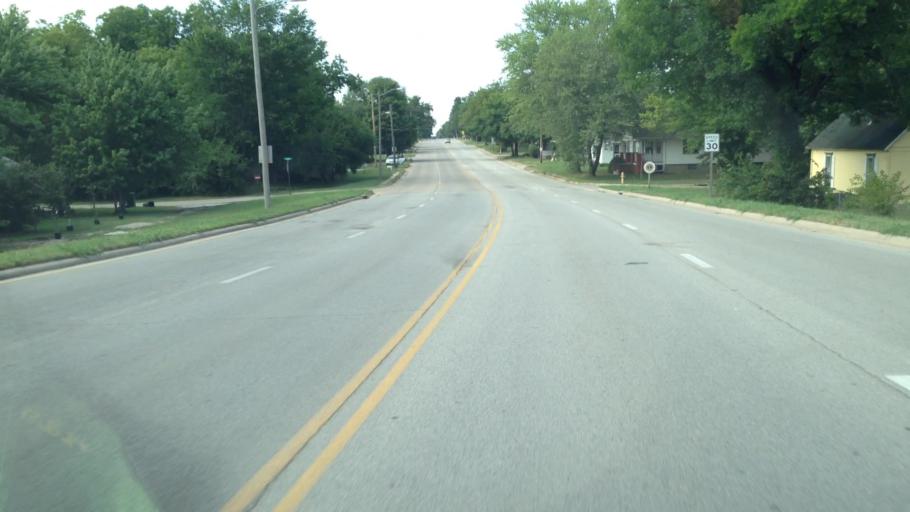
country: US
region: Kansas
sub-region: Labette County
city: Parsons
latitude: 37.3296
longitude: -95.2593
